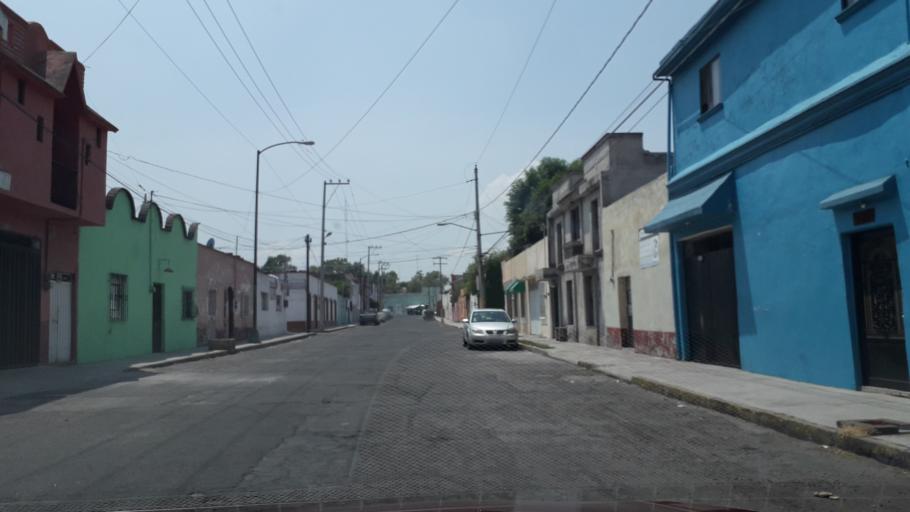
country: MX
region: Puebla
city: Puebla
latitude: 19.0511
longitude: -98.1882
